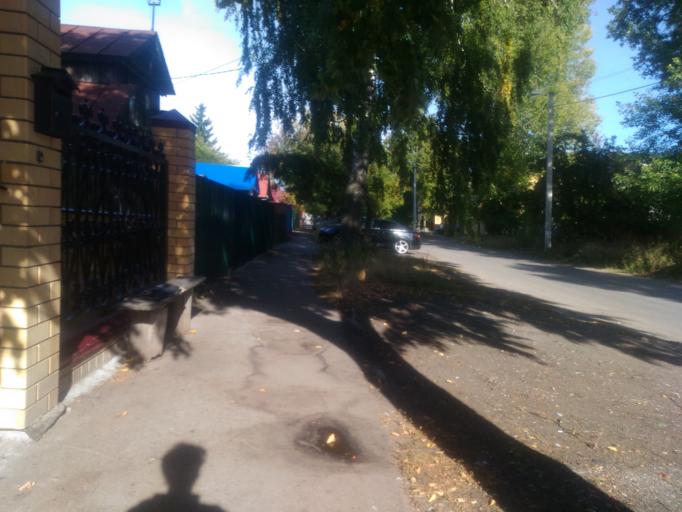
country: RU
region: Ulyanovsk
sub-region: Ulyanovskiy Rayon
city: Ulyanovsk
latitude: 54.3492
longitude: 48.3791
